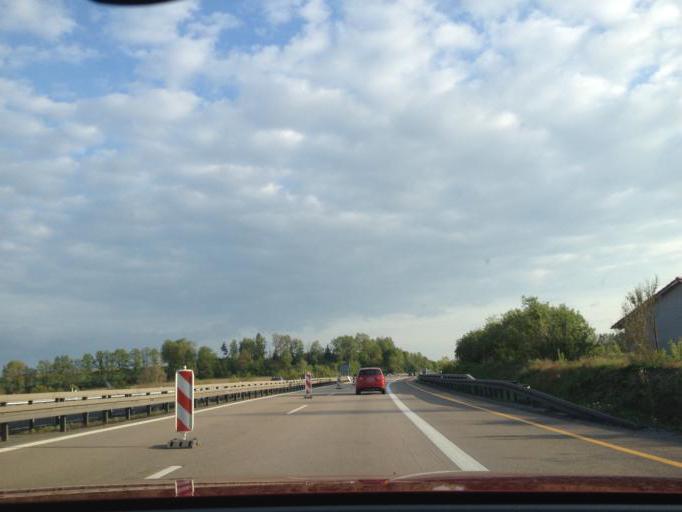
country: DE
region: Bavaria
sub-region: Upper Palatinate
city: Windischeschenbach
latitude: 49.8037
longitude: 12.1821
